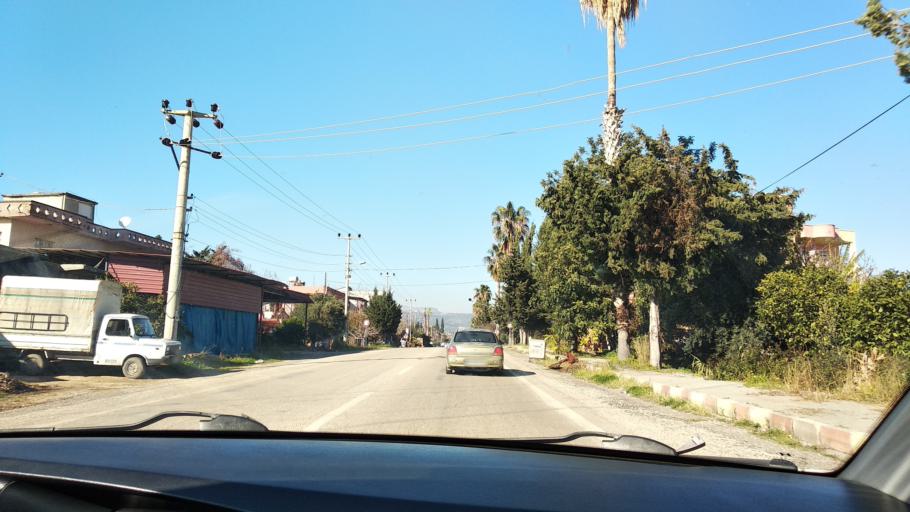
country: TR
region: Mersin
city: Tomuk
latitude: 36.6592
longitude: 34.3651
